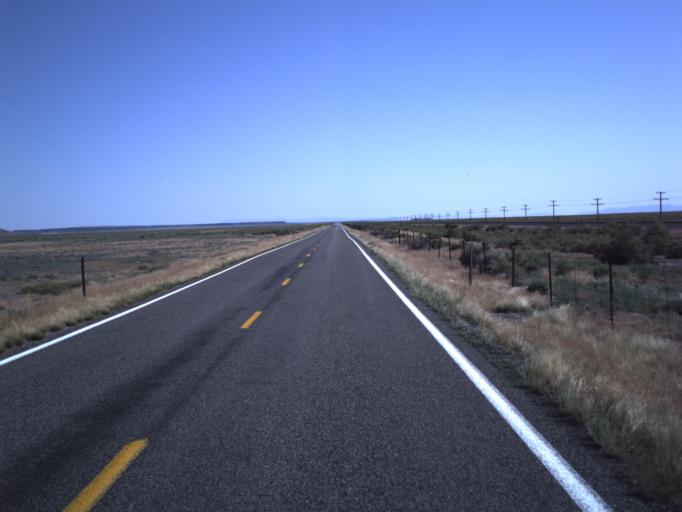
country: US
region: Utah
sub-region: Millard County
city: Delta
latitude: 39.0517
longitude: -112.7669
